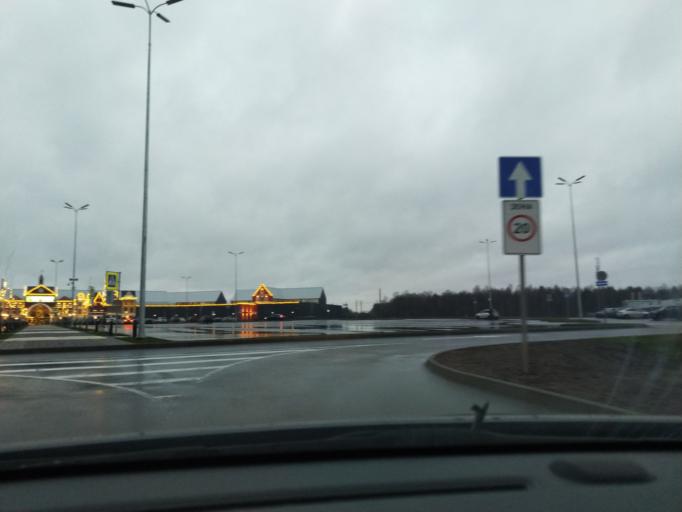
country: RU
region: St.-Petersburg
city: Gorelovo
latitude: 59.7934
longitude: 30.1478
